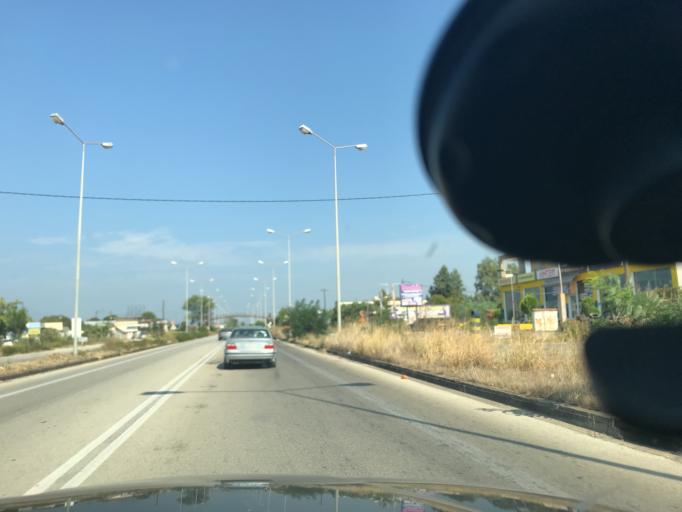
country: GR
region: West Greece
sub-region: Nomos Ileias
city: Pyrgos
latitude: 37.6860
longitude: 21.4122
